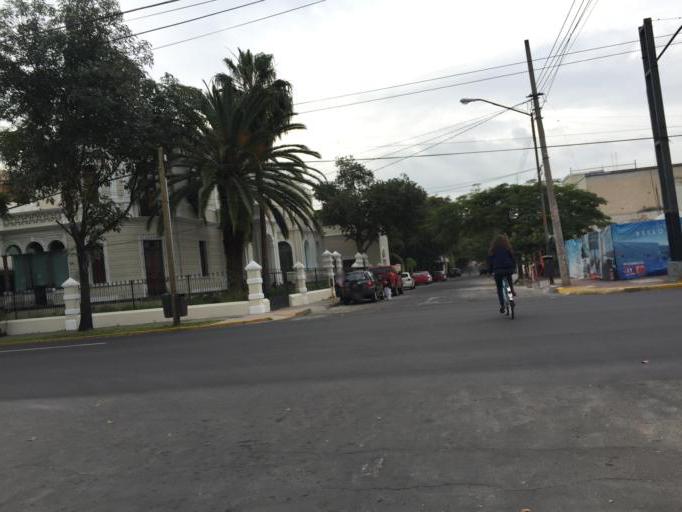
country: MX
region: Jalisco
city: Guadalajara
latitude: 20.6771
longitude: -103.3651
